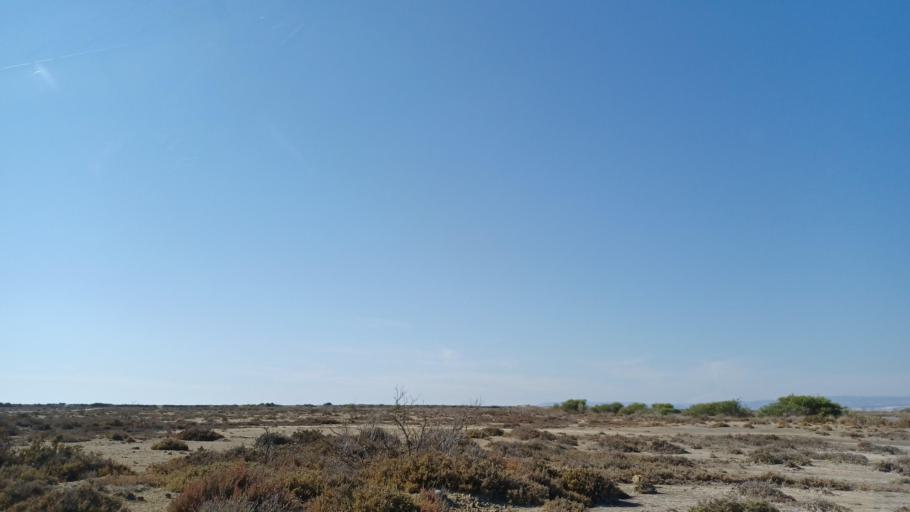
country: CY
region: Larnaka
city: Kolossi
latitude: 34.6080
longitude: 32.9370
